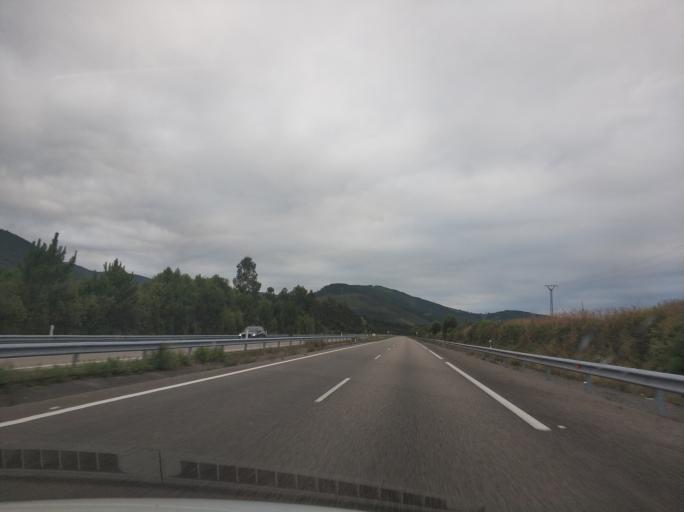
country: ES
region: Asturias
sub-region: Province of Asturias
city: Tineo
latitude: 43.5444
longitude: -6.4719
